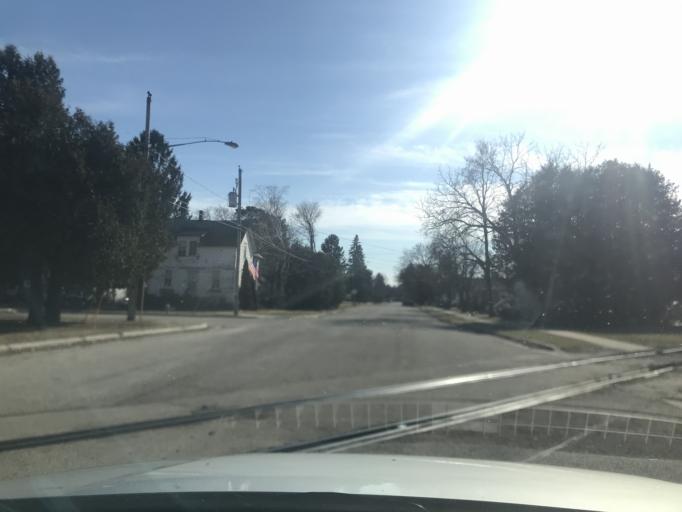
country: US
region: Wisconsin
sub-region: Marinette County
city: Marinette
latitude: 45.0962
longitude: -87.6413
